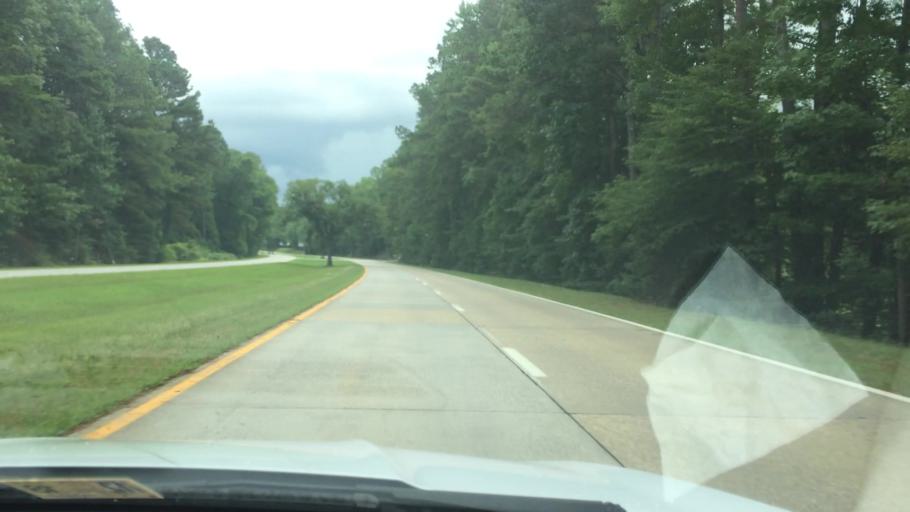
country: US
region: Virginia
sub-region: King William County
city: West Point
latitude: 37.4064
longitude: -76.8521
